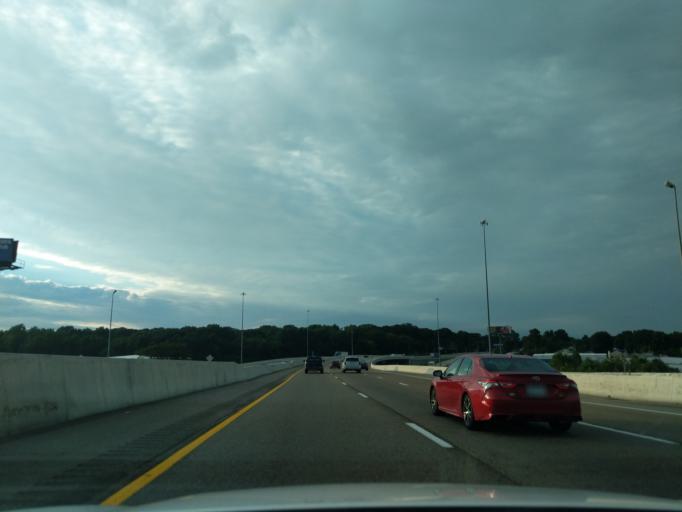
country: US
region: Tennessee
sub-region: Shelby County
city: New South Memphis
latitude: 35.0849
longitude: -90.0755
